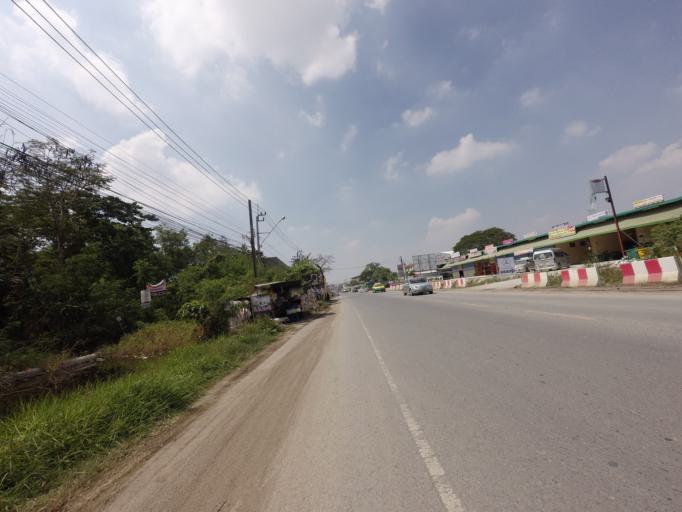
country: TH
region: Bangkok
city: Suan Luang
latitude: 13.7473
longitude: 100.6587
